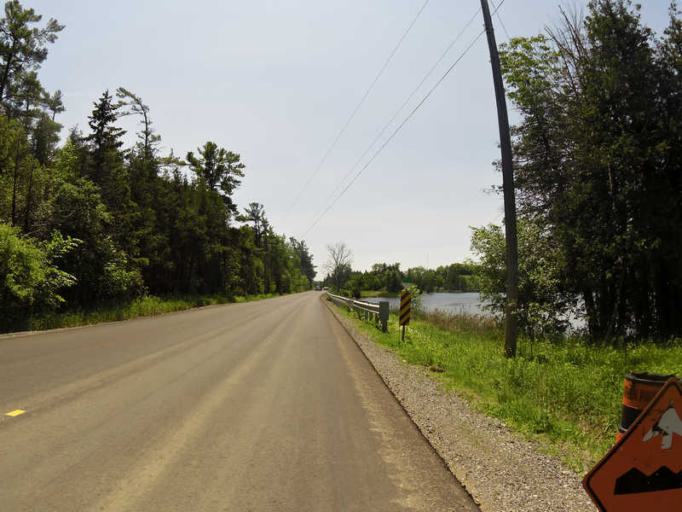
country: CA
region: Ontario
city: Peterborough
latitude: 44.3695
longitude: -78.2904
